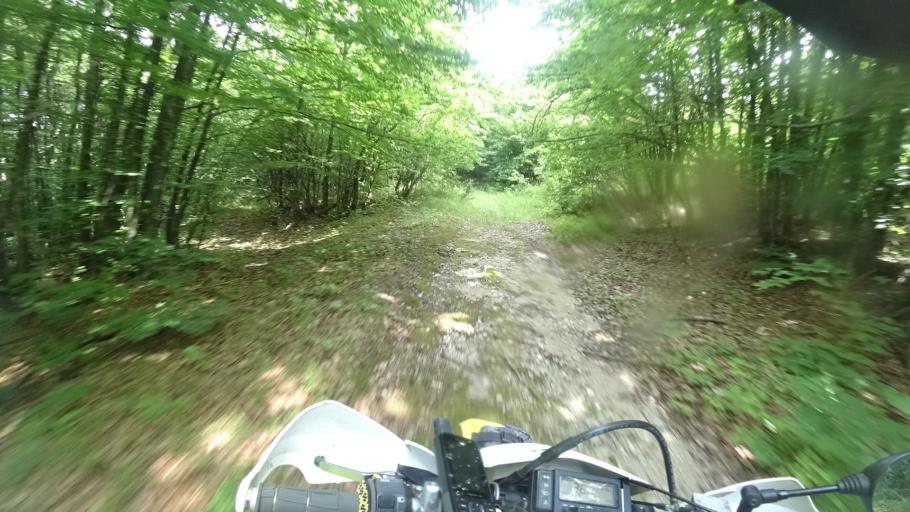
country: BA
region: Federation of Bosnia and Herzegovina
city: Izacic
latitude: 44.8730
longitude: 15.7037
